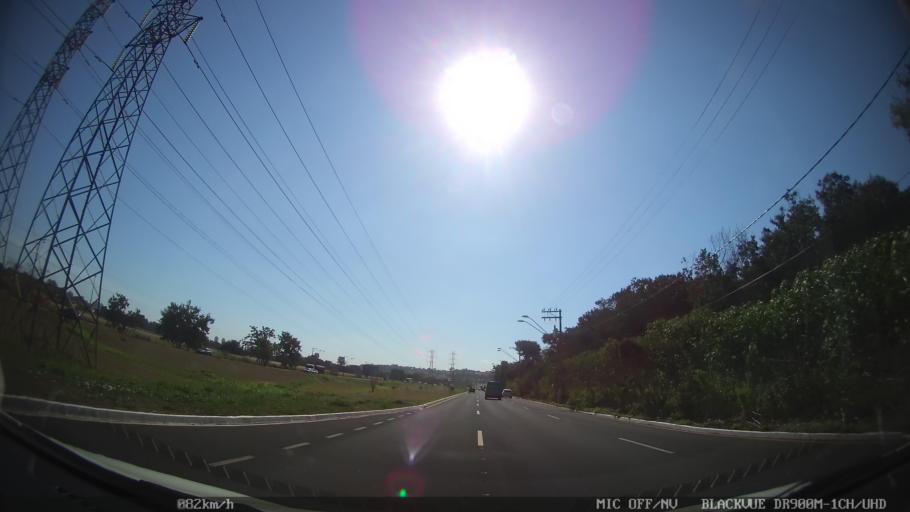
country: BR
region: Sao Paulo
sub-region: Ribeirao Preto
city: Ribeirao Preto
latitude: -21.2202
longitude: -47.7703
